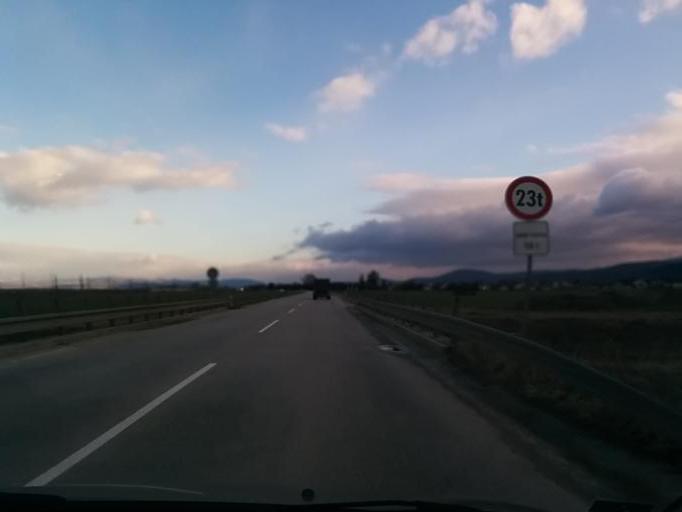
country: SK
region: Nitriansky
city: Cachtice
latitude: 48.6674
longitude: 17.8433
